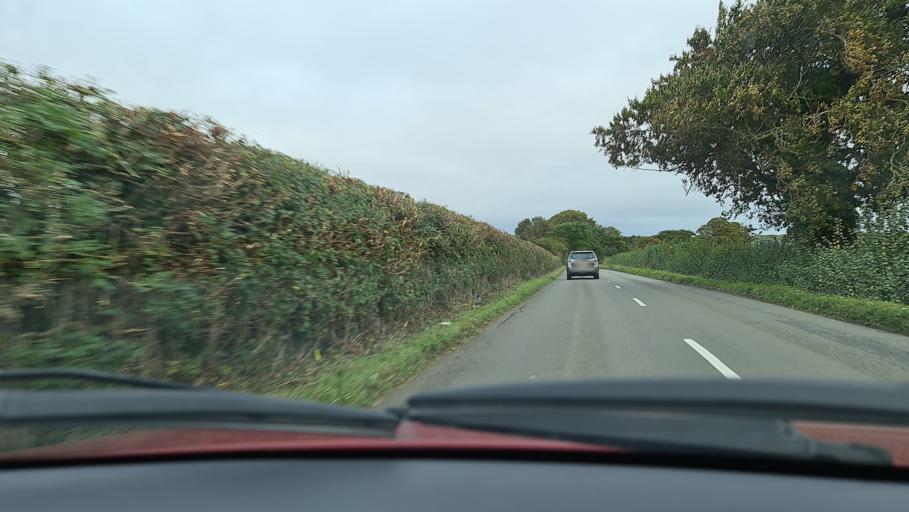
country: GB
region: England
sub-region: Oxfordshire
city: Somerton
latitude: 51.9182
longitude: -1.2392
